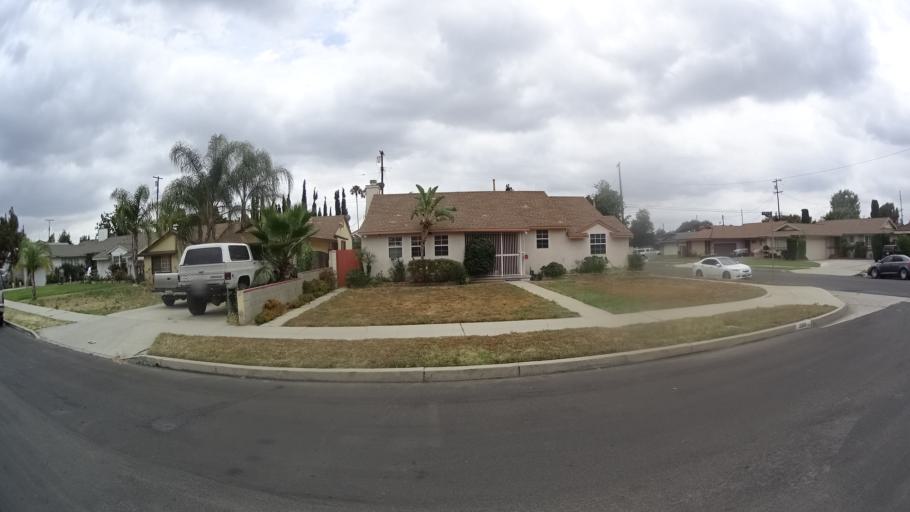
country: US
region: California
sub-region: Los Angeles County
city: San Fernando
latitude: 34.2628
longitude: -118.4656
